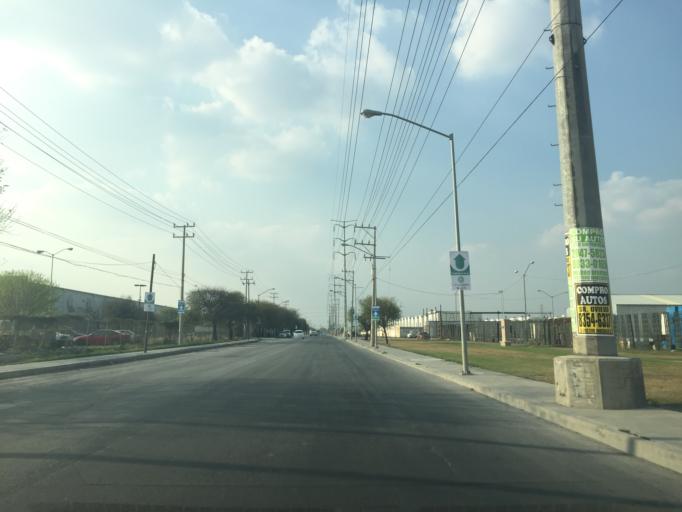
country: MX
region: Nuevo Leon
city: Apodaca
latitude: 25.7650
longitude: -100.2097
